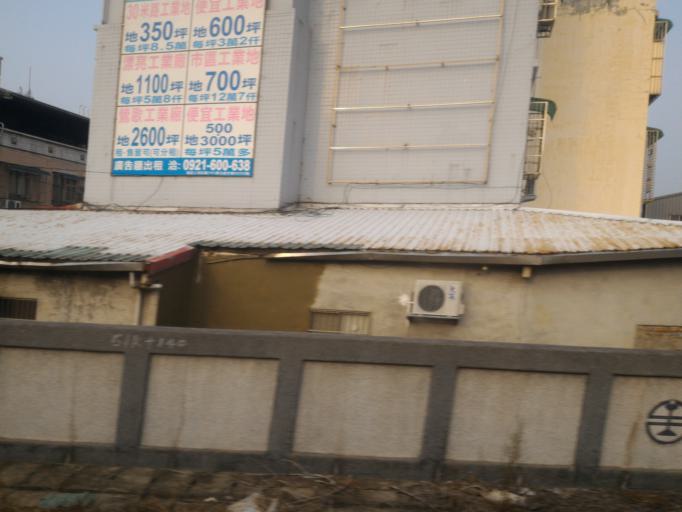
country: TW
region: Taiwan
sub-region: Taoyuan
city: Taoyuan
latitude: 24.9488
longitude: 121.3384
